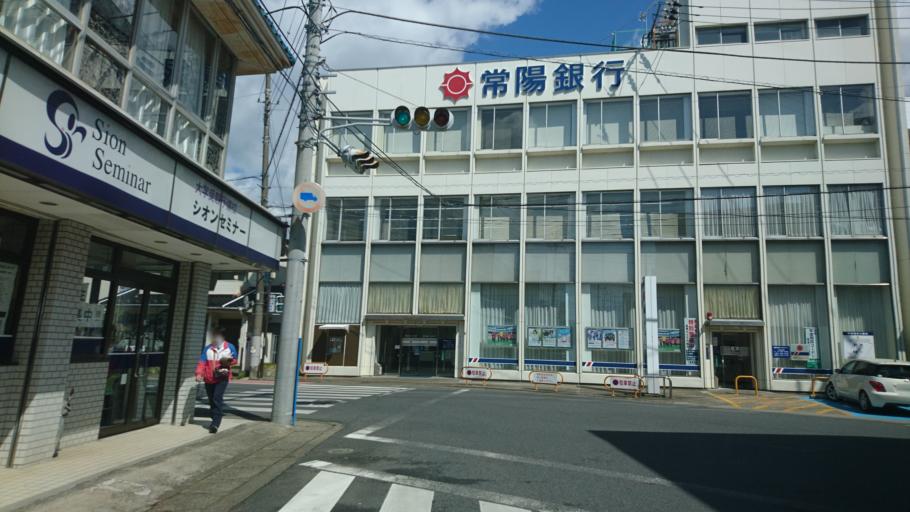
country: JP
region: Ibaraki
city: Ishige
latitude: 36.1820
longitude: 139.9584
